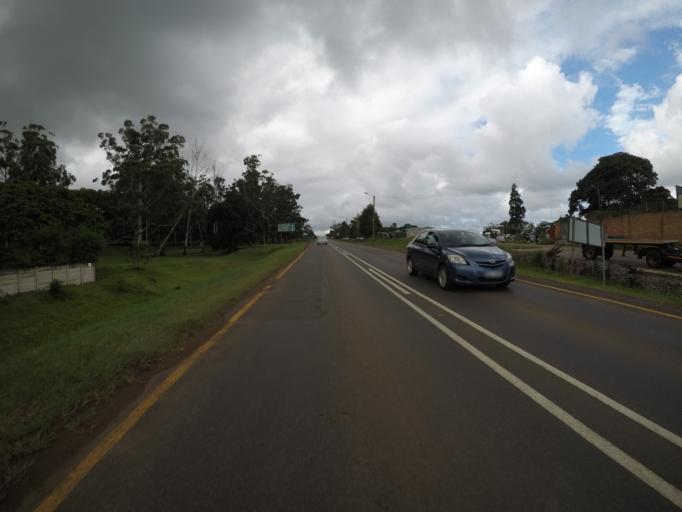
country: ZA
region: KwaZulu-Natal
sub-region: uMkhanyakude District Municipality
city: Mtubatuba
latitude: -28.4116
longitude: 32.1841
